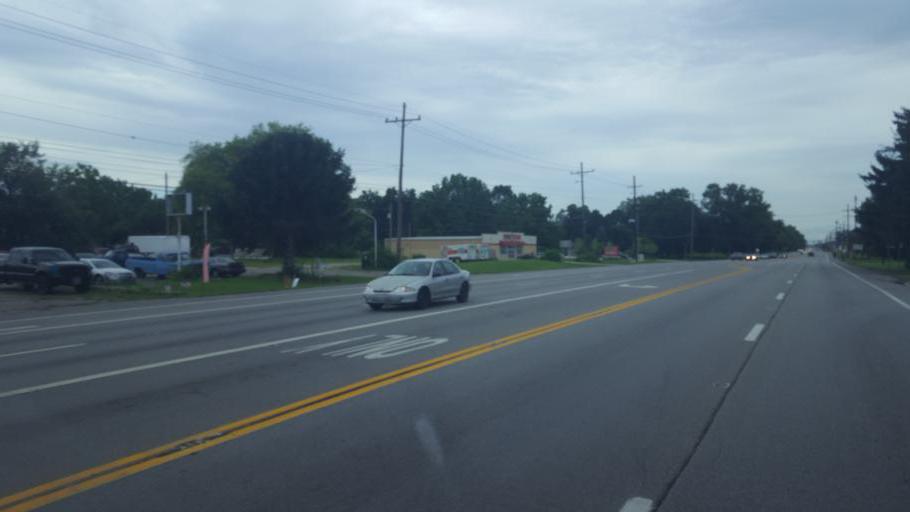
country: US
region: Ohio
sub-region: Franklin County
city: Blacklick Estates
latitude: 39.9003
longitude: -82.8820
